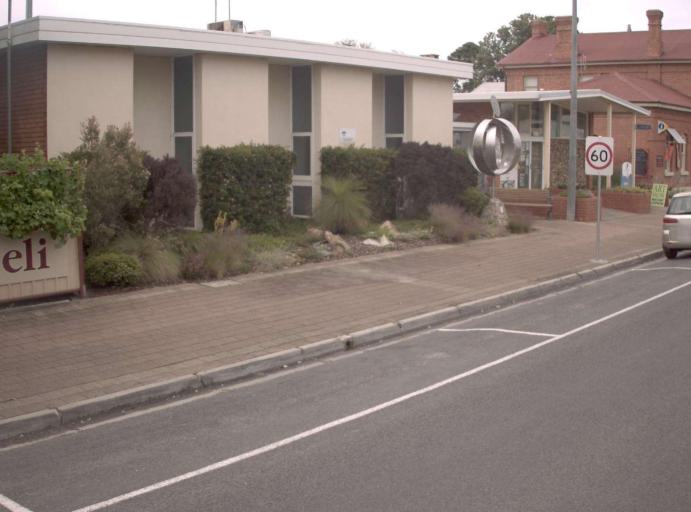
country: AU
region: Victoria
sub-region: Wellington
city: Sale
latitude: -37.9654
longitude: 147.0802
